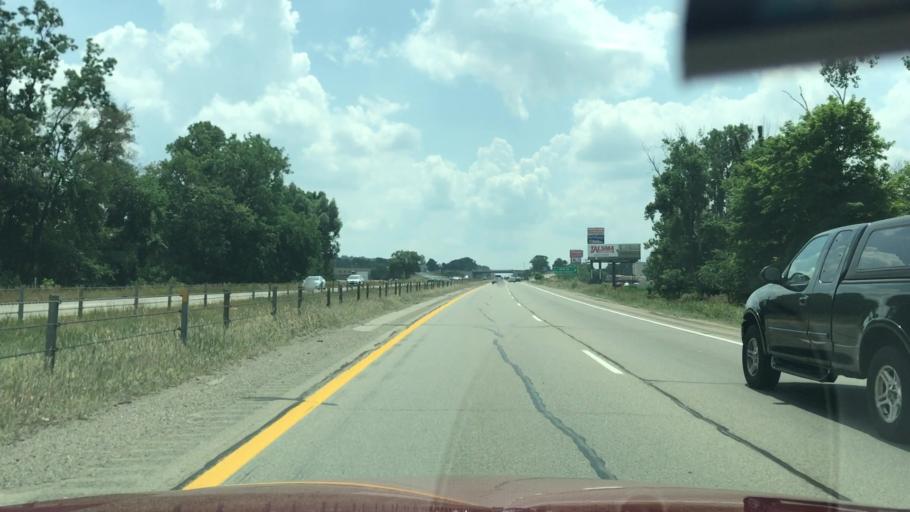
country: US
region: Michigan
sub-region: Kent County
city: Cutlerville
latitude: 42.8183
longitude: -85.6690
